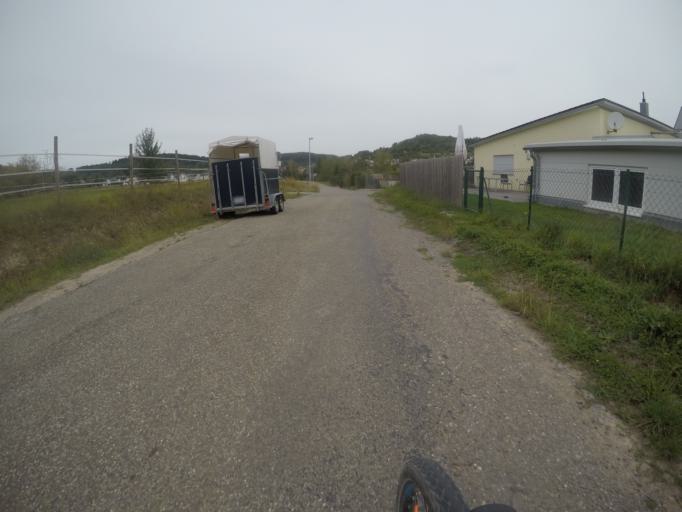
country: DE
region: Baden-Wuerttemberg
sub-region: Karlsruhe Region
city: Simmozheim
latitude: 48.7735
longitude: 8.8265
